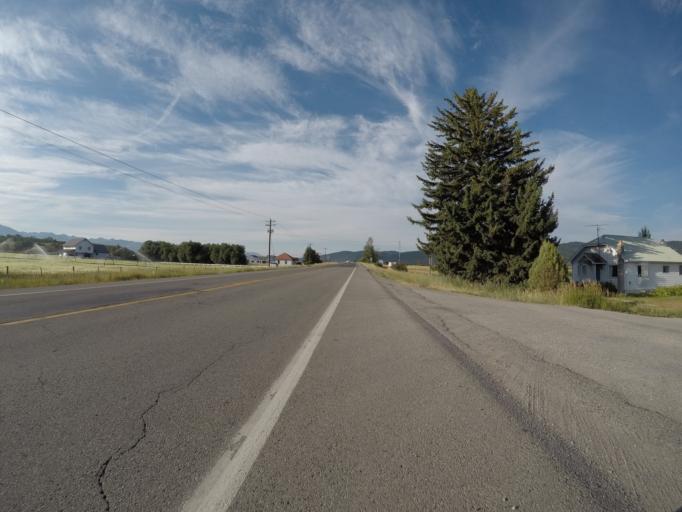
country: US
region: Wyoming
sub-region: Lincoln County
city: Afton
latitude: 42.9316
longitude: -111.0074
